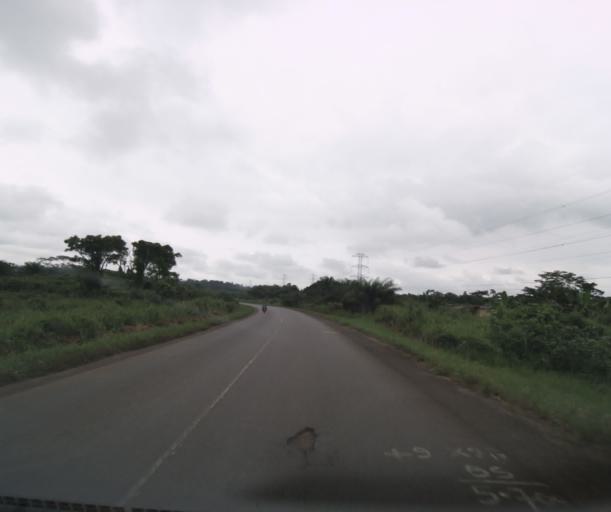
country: CM
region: Littoral
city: Edea
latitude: 3.7462
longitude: 10.1183
